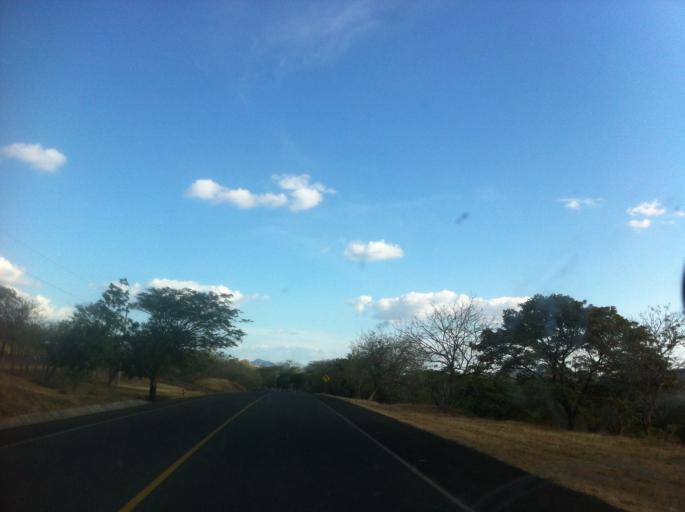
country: NI
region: Chontales
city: Acoyapa
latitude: 11.9559
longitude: -85.1615
